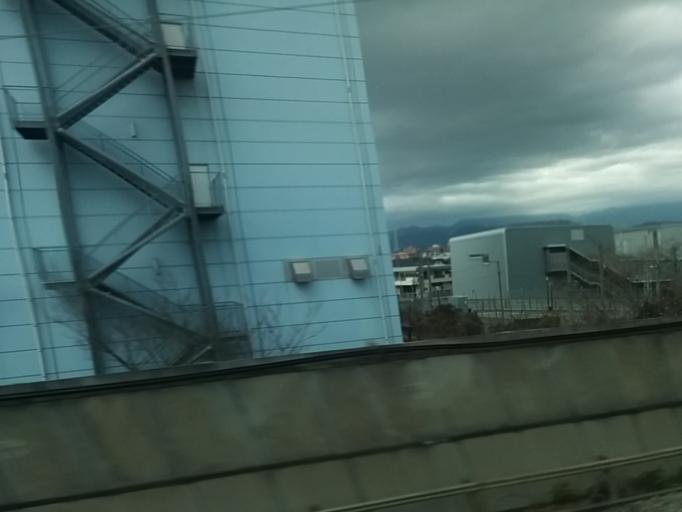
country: JP
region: Kanagawa
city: Odawara
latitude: 35.2728
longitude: 139.1715
